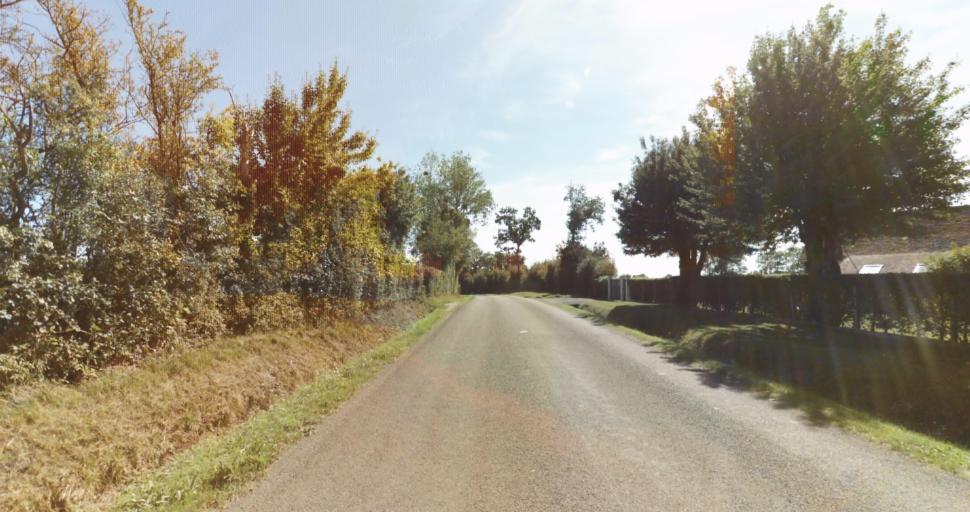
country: FR
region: Lower Normandy
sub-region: Departement de l'Orne
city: Gace
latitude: 48.7495
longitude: 0.2661
